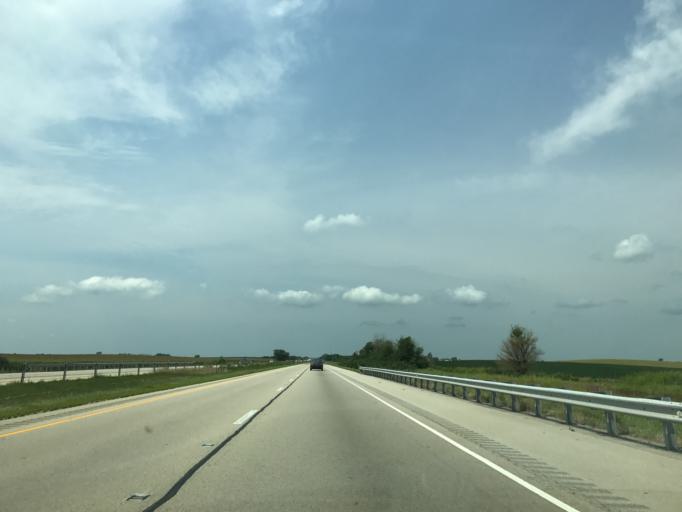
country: US
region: Illinois
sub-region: LaSalle County
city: Marseilles
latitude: 41.3758
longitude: -88.6534
